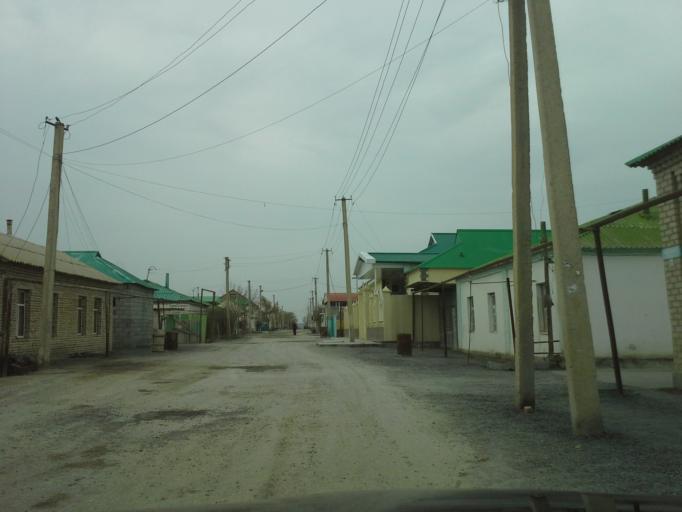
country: TM
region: Ahal
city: Abadan
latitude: 37.9753
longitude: 58.2202
